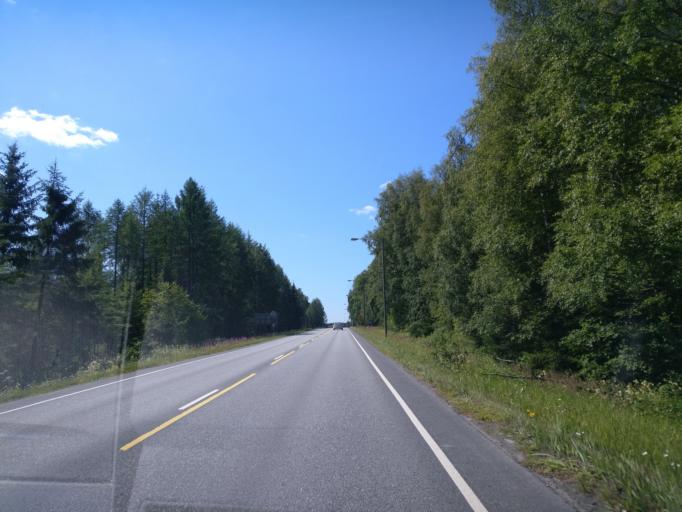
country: FI
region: Satakunta
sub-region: Pori
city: Kullaa
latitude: 61.4638
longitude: 22.1605
